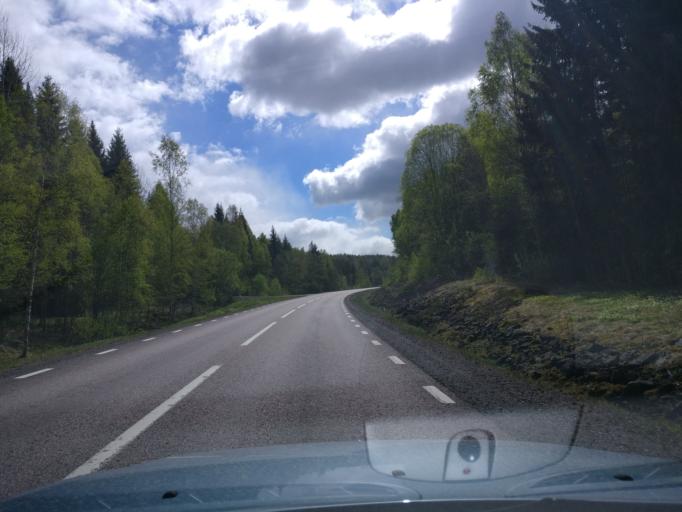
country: SE
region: Vaermland
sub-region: Karlstads Kommun
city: Molkom
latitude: 59.6597
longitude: 13.7088
